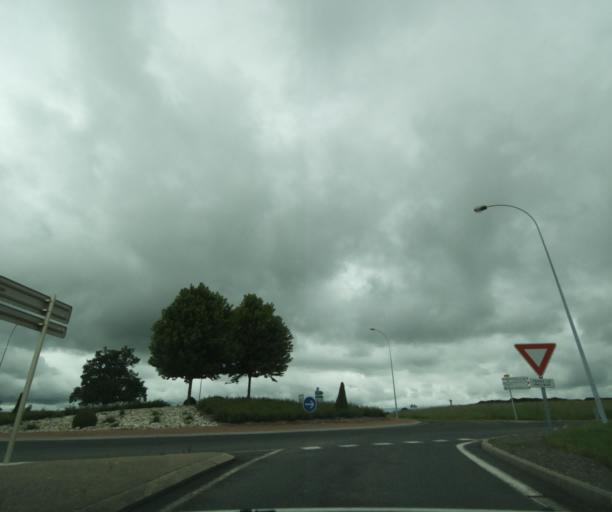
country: FR
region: Bourgogne
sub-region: Departement de Saone-et-Loire
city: Charolles
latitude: 46.4400
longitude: 4.3008
